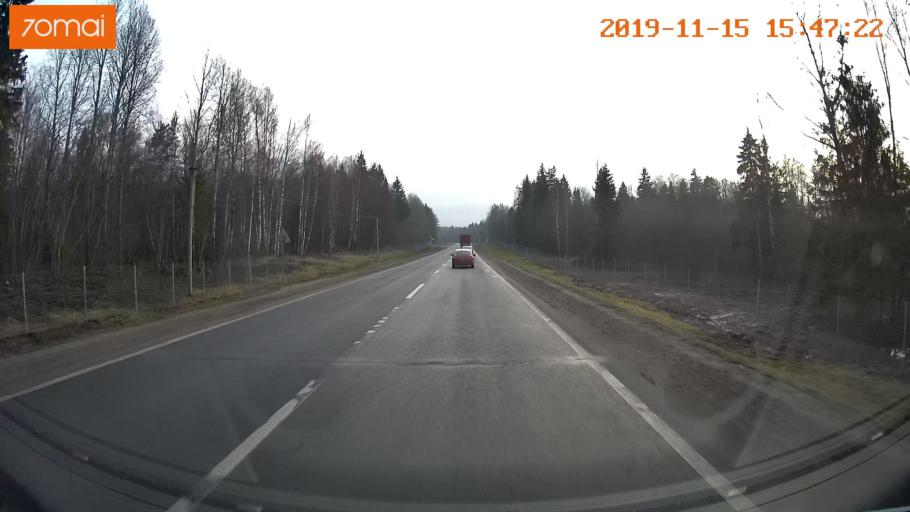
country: RU
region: Jaroslavl
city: Danilov
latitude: 57.9389
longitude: 40.0102
